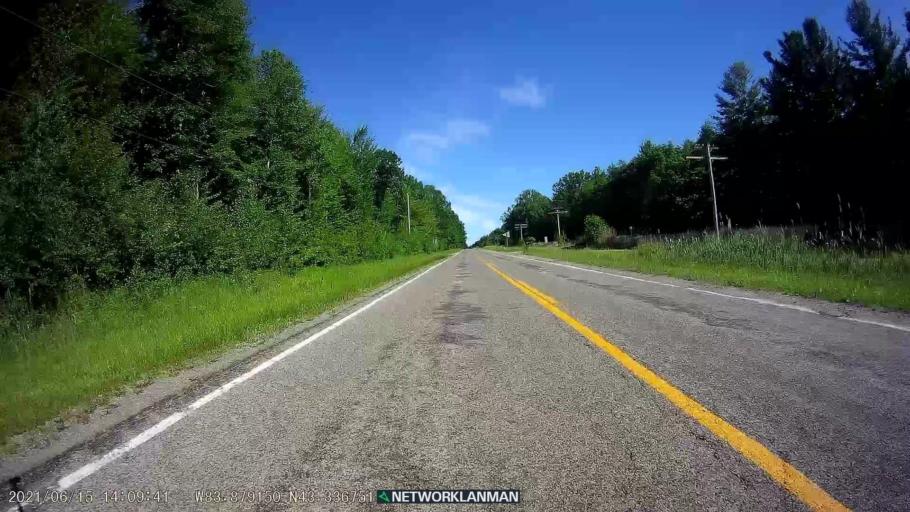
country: US
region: Michigan
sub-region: Saginaw County
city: Bridgeport
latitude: 43.3369
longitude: -83.8793
